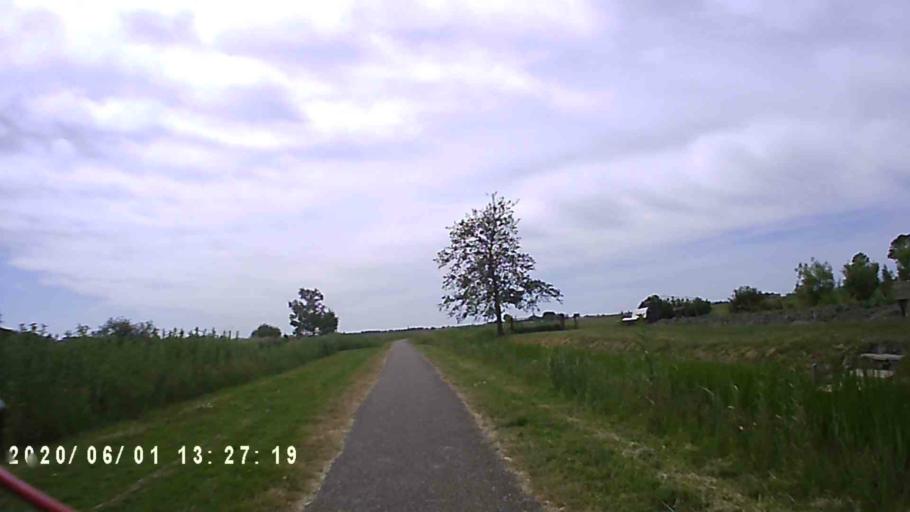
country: NL
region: Friesland
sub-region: Gemeente Littenseradiel
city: Wommels
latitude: 53.1045
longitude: 5.5811
